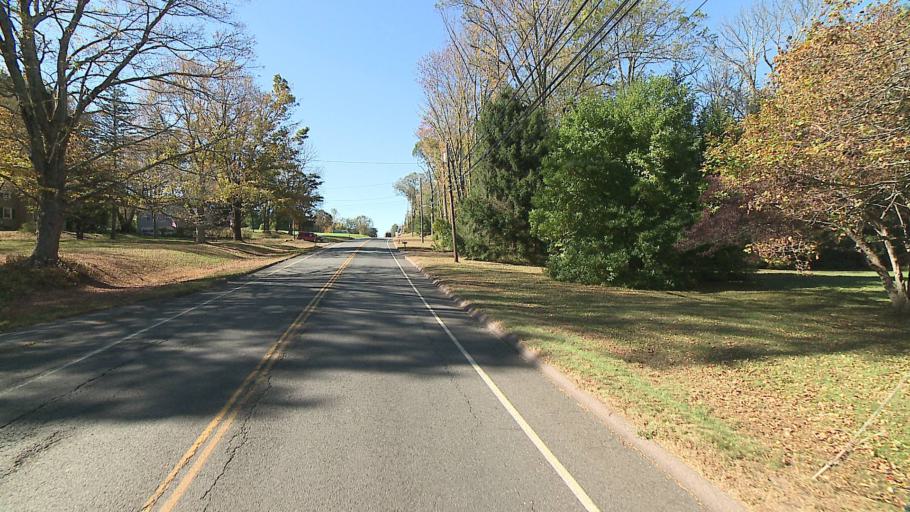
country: US
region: Connecticut
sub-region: Tolland County
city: South Coventry
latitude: 41.7048
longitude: -72.2956
